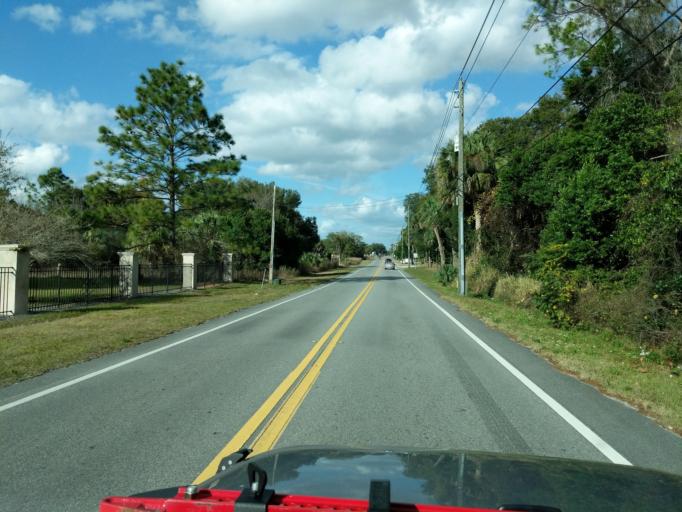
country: US
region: Florida
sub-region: Seminole County
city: Geneva
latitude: 28.7285
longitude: -81.1150
